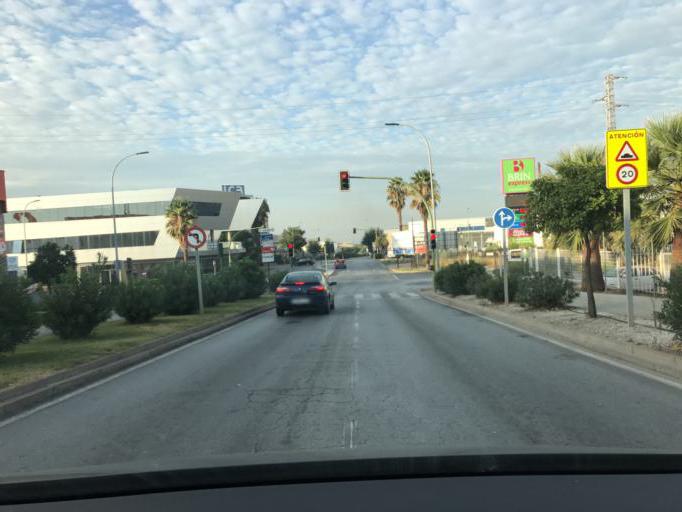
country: ES
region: Andalusia
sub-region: Provincia de Granada
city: Peligros
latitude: 37.2268
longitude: -3.6403
